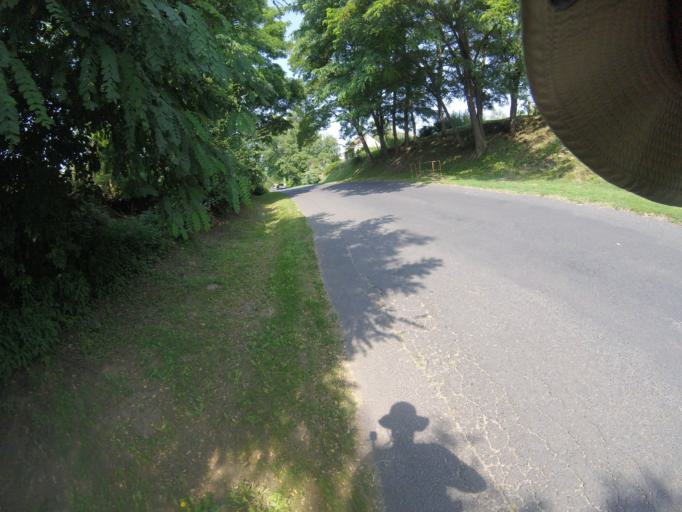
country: HU
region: Veszprem
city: Badacsonytomaj
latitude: 46.7998
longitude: 17.4444
